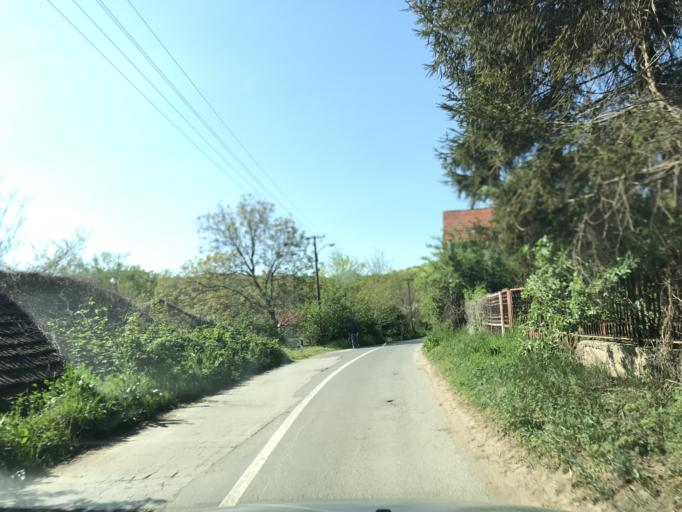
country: RS
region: Central Serbia
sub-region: Nisavski Okrug
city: Nis
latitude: 43.4088
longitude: 21.8200
